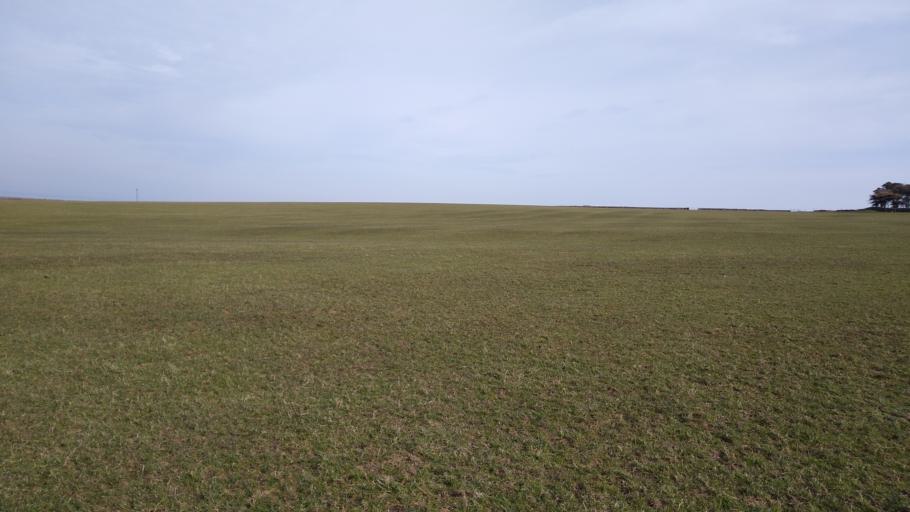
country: GB
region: England
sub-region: Cumbria
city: Cockermouth
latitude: 54.7140
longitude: -3.3525
